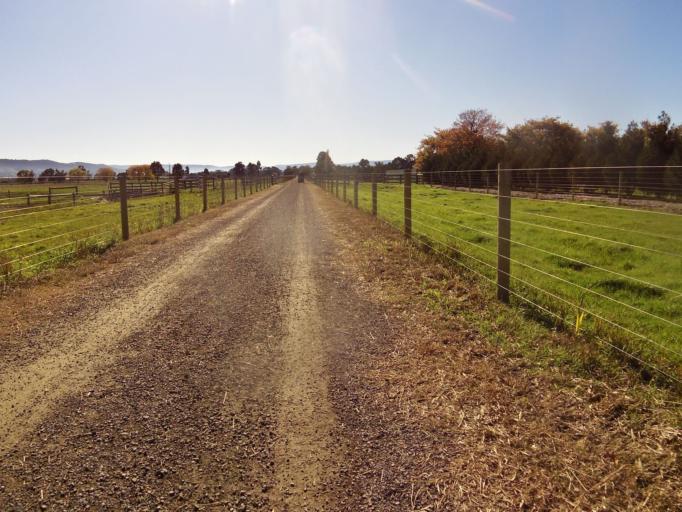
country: AU
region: Victoria
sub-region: Yarra Ranges
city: Yarra Glen
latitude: -37.7035
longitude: 145.3708
